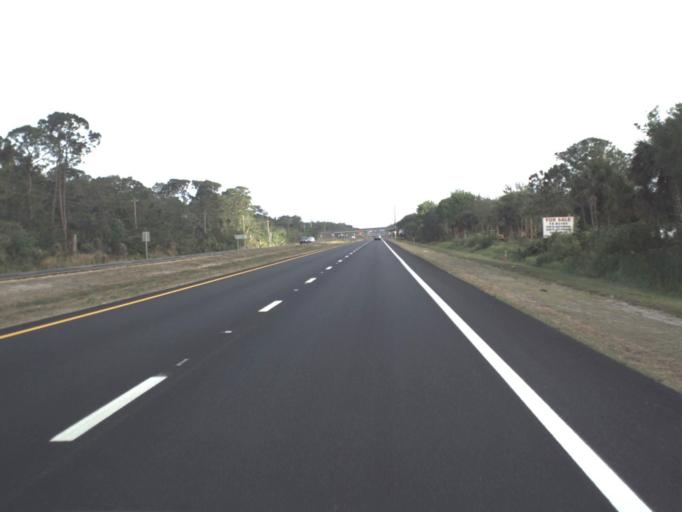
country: US
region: Florida
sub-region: Brevard County
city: Port Saint John
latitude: 28.5357
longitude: -80.7922
